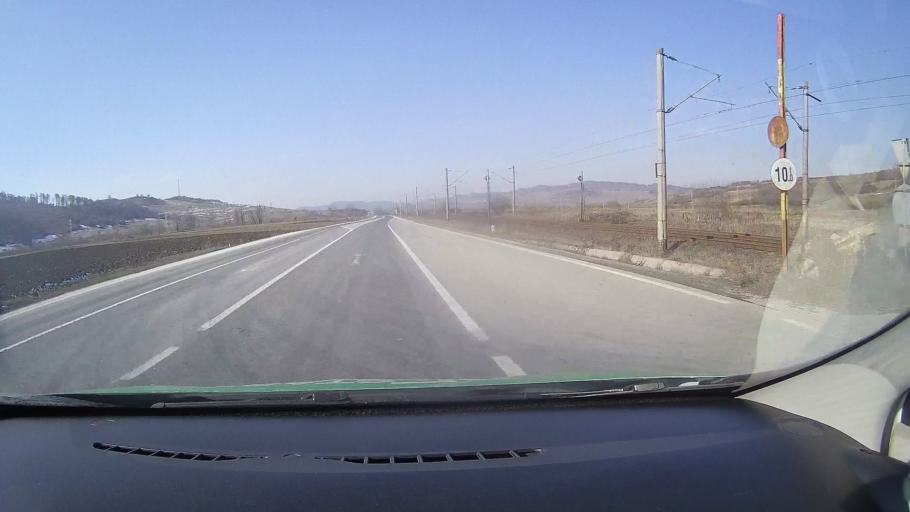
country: RO
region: Mures
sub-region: Comuna Vanatori
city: Vanatori
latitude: 46.2312
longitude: 24.9754
